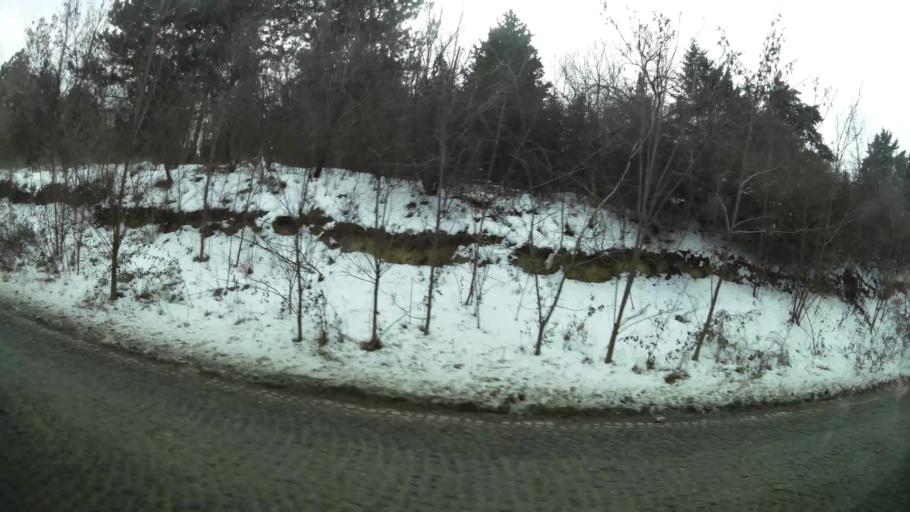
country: MK
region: Suto Orizari
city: Suto Orizare
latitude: 42.0430
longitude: 21.4365
